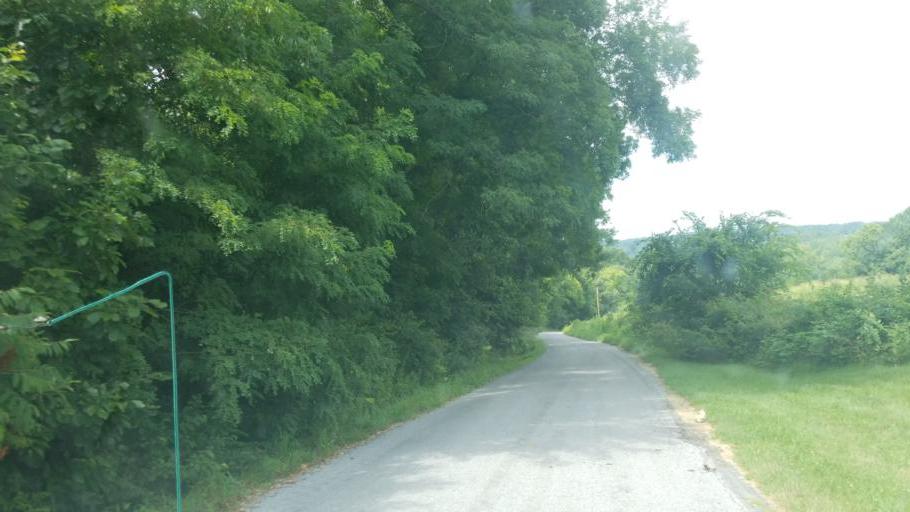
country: US
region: Illinois
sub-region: Union County
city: Cobden
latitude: 37.6135
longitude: -89.3429
